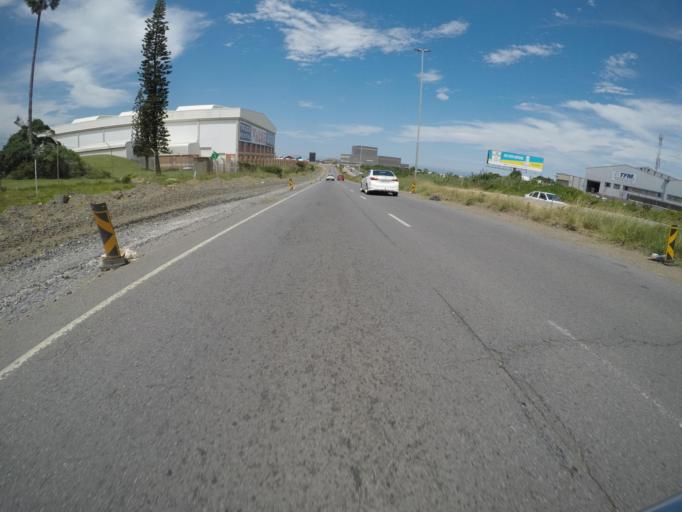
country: ZA
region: Eastern Cape
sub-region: Buffalo City Metropolitan Municipality
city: East London
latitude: -33.0360
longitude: 27.8713
